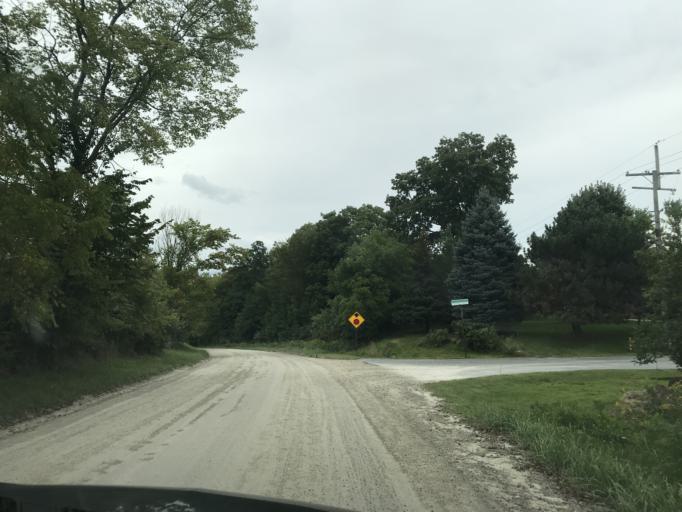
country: US
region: Michigan
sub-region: Washtenaw County
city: Ann Arbor
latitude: 42.3316
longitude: -83.6644
